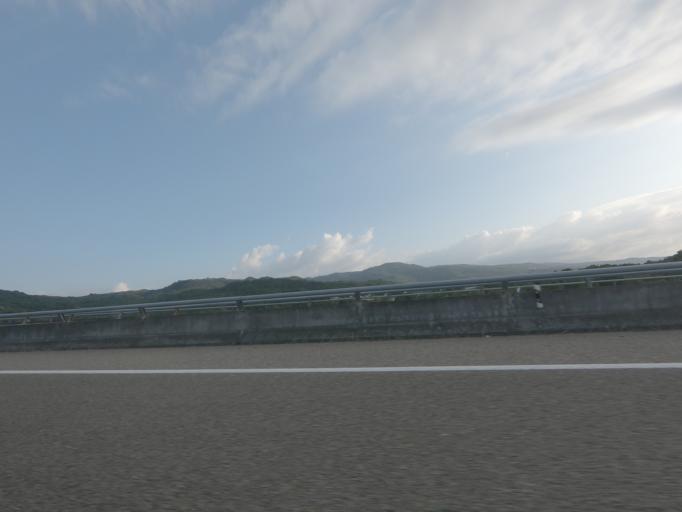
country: ES
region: Galicia
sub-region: Provincia de Ourense
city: Allariz
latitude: 42.1968
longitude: -7.7794
